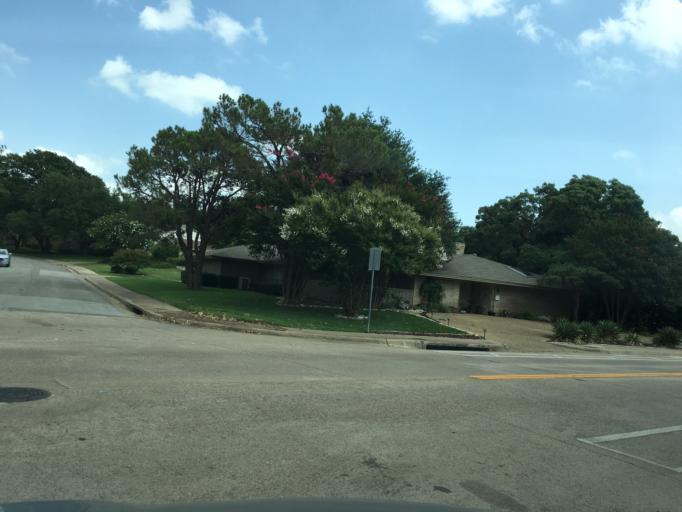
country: US
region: Texas
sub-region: Dallas County
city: University Park
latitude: 32.8874
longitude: -96.7771
